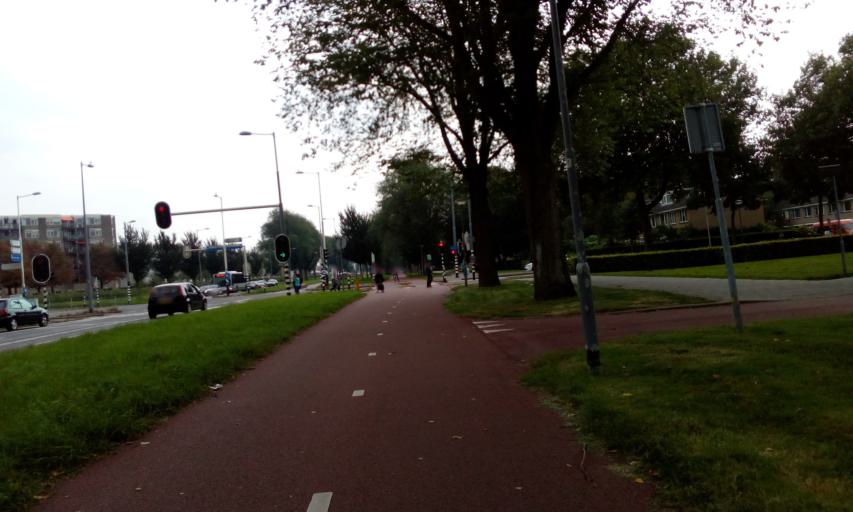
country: NL
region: South Holland
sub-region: Gemeente Rotterdam
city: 's-Gravenland
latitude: 51.9454
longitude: 4.5538
